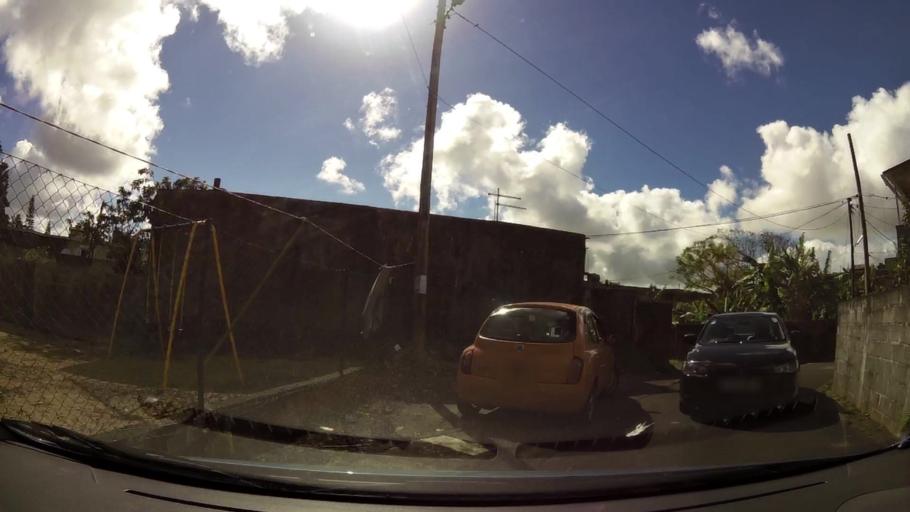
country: MU
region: Plaines Wilhems
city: Curepipe
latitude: -20.3300
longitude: 57.5186
